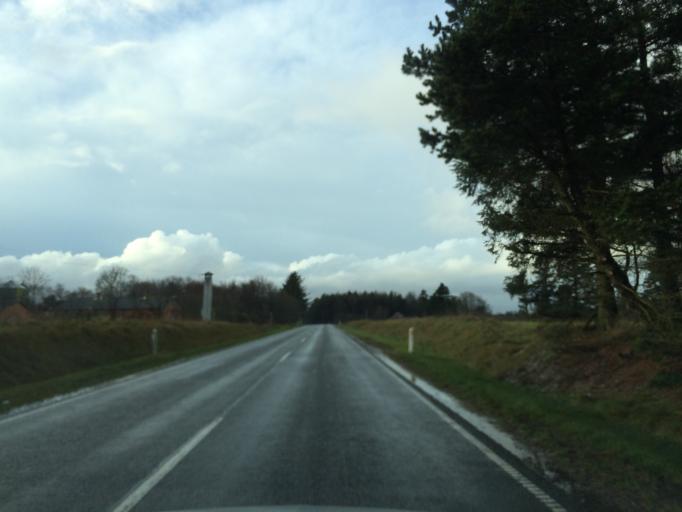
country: DK
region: Central Jutland
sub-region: Holstebro Kommune
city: Ulfborg
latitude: 56.1986
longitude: 8.3921
